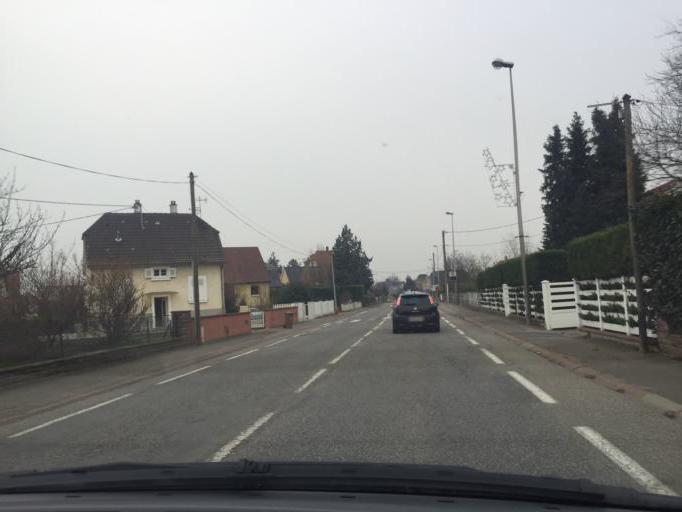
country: FR
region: Alsace
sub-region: Departement du Haut-Rhin
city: Horbourg-Wihr
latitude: 48.0783
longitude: 7.4017
